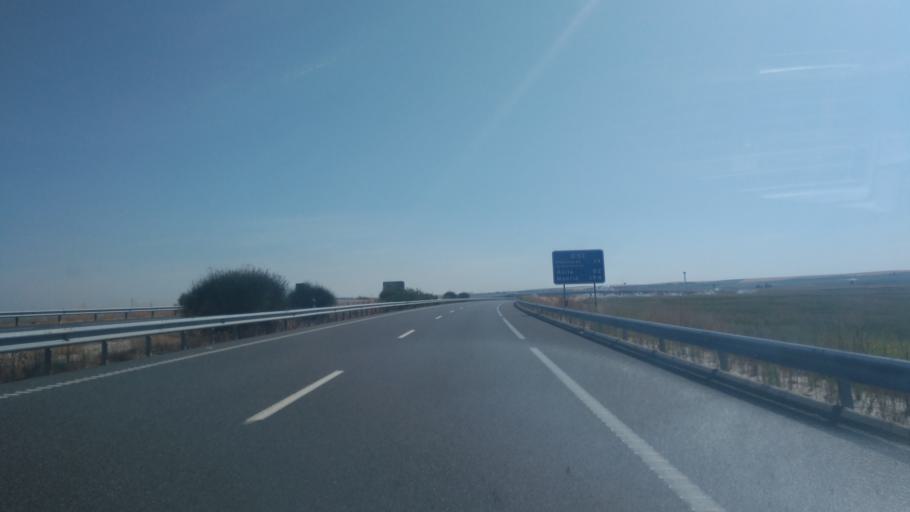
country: ES
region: Castille and Leon
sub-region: Provincia de Salamanca
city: Encinas de Abajo
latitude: 40.9308
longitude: -5.4540
